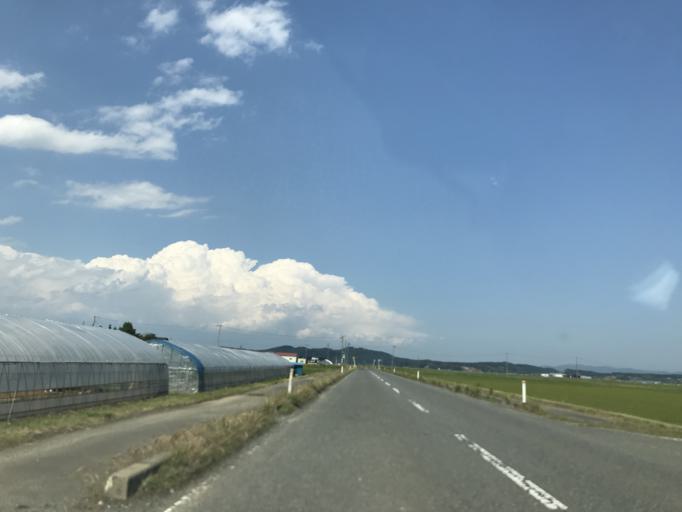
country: JP
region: Miyagi
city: Wakuya
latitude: 38.4593
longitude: 141.1217
